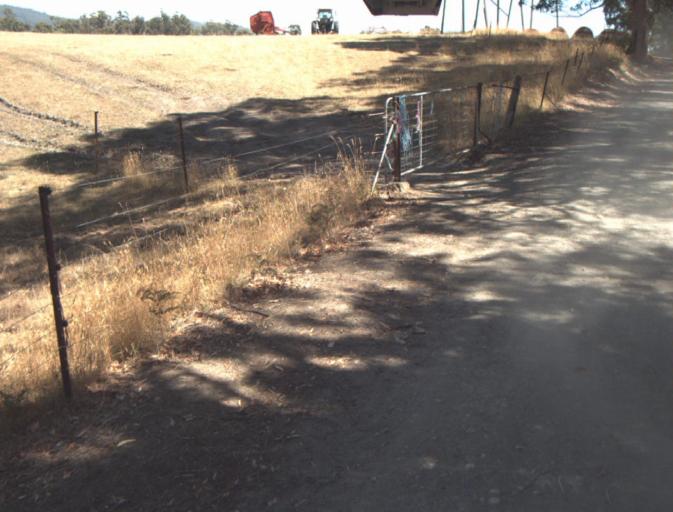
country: AU
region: Tasmania
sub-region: Launceston
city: Mayfield
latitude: -41.2494
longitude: 147.1732
